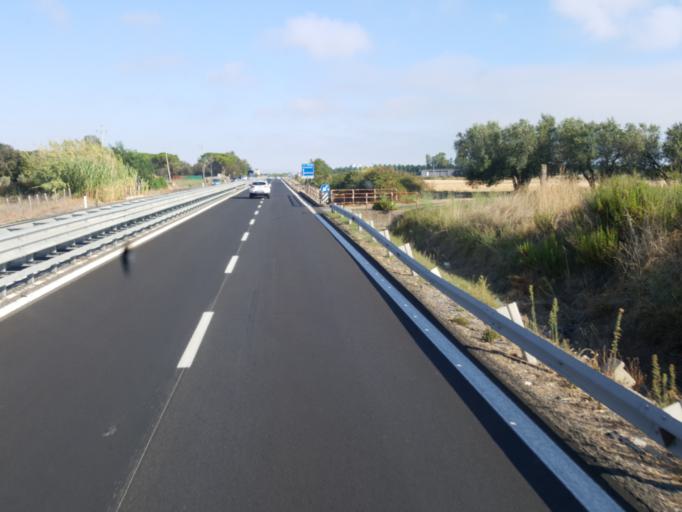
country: IT
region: Latium
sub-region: Provincia di Viterbo
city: Montalto di Castro
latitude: 42.3320
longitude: 11.6275
